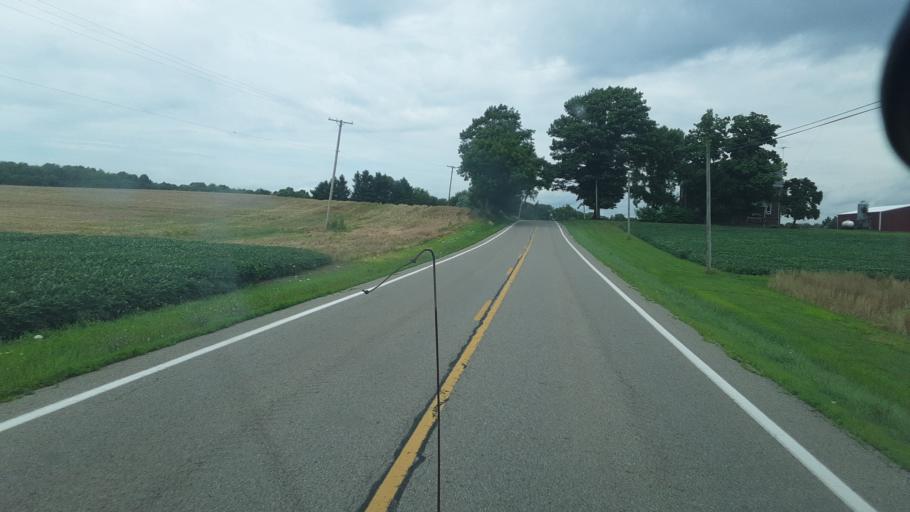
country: US
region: Ohio
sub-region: Trumbull County
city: Cortland
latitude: 41.4394
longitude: -80.6655
